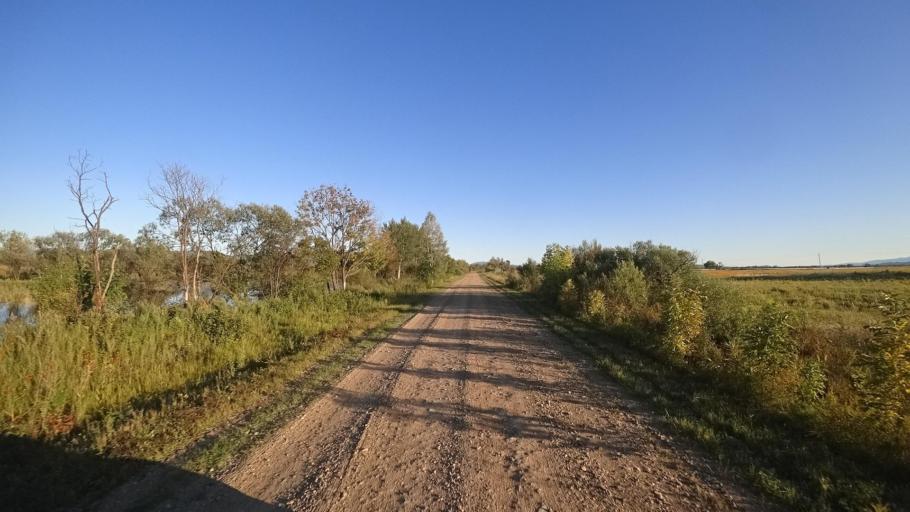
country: RU
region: Primorskiy
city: Kirovskiy
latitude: 44.8073
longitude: 133.6175
